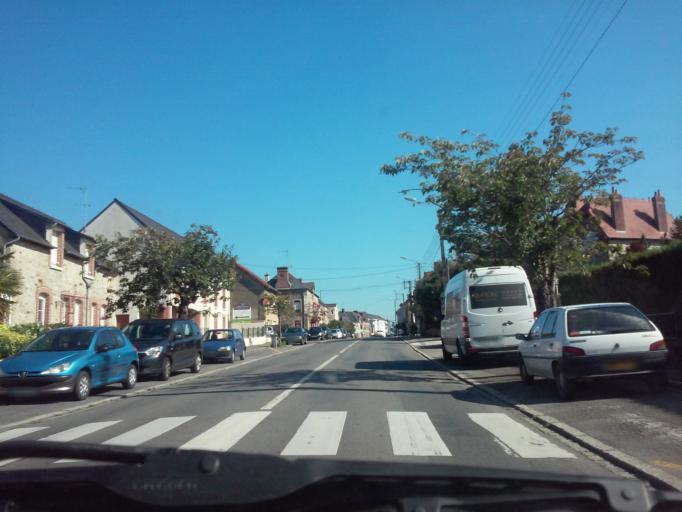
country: FR
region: Brittany
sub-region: Departement d'Ille-et-Vilaine
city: Betton
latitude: 48.1792
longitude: -1.6381
